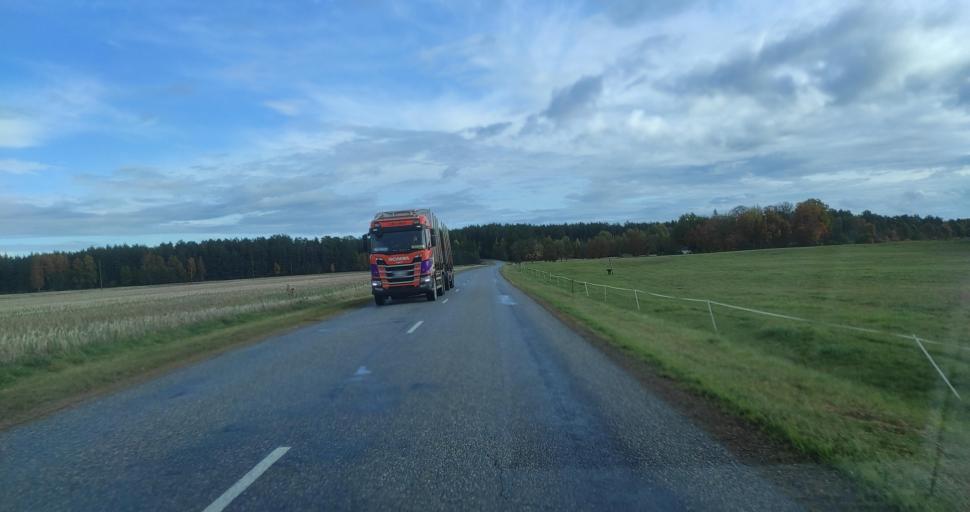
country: LV
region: Skrunda
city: Skrunda
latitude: 56.6298
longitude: 21.9933
